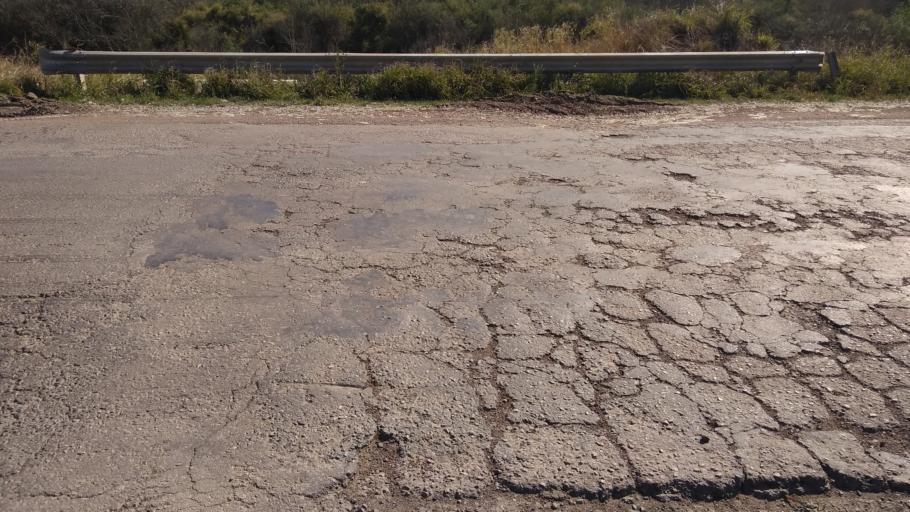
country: AR
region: Santiago del Estero
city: Los Juries
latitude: -28.6001
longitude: -61.5170
